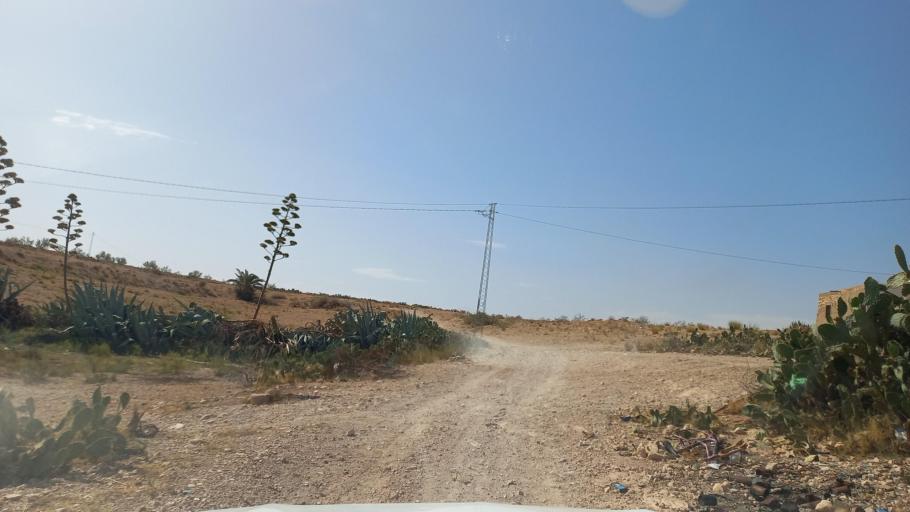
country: TN
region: Al Qasrayn
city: Kasserine
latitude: 35.2714
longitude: 8.9546
